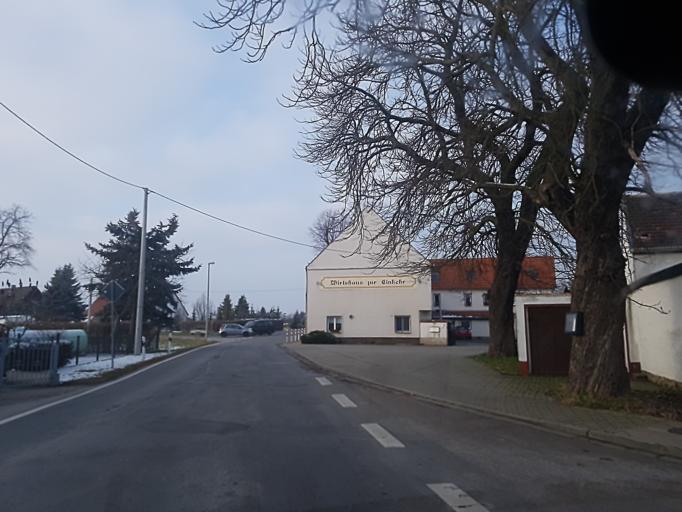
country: DE
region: Saxony
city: Oschatz
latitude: 51.3412
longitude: 13.0924
